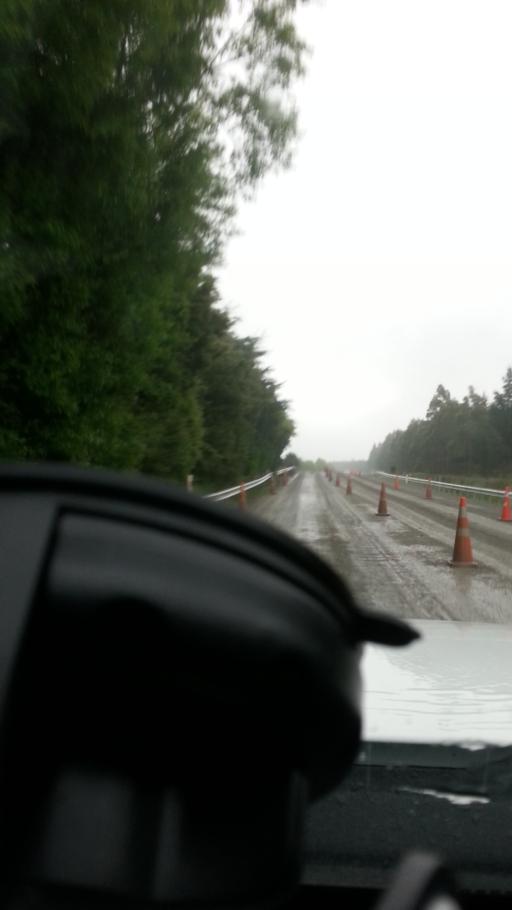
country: NZ
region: Wellington
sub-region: Masterton District
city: Masterton
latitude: -40.8081
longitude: 175.6201
